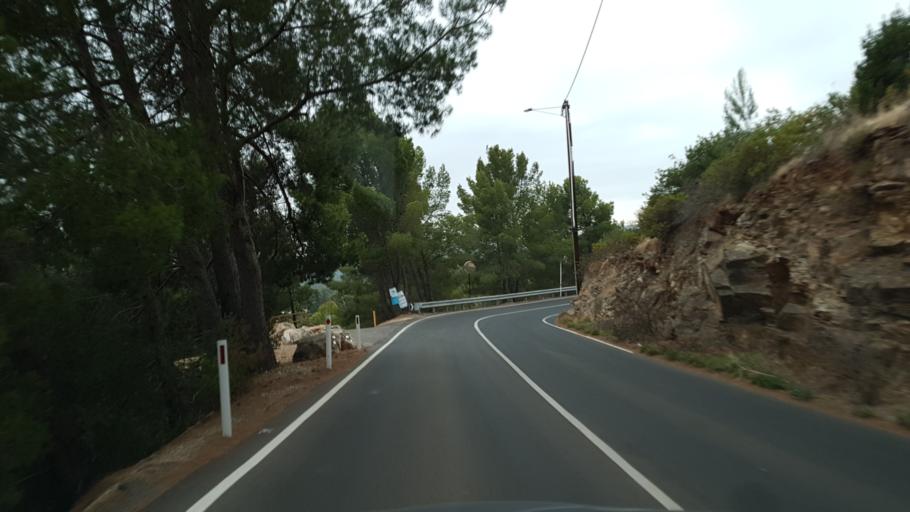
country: AU
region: South Australia
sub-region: Burnside
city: Mount Osmond
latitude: -34.9612
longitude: 138.6519
